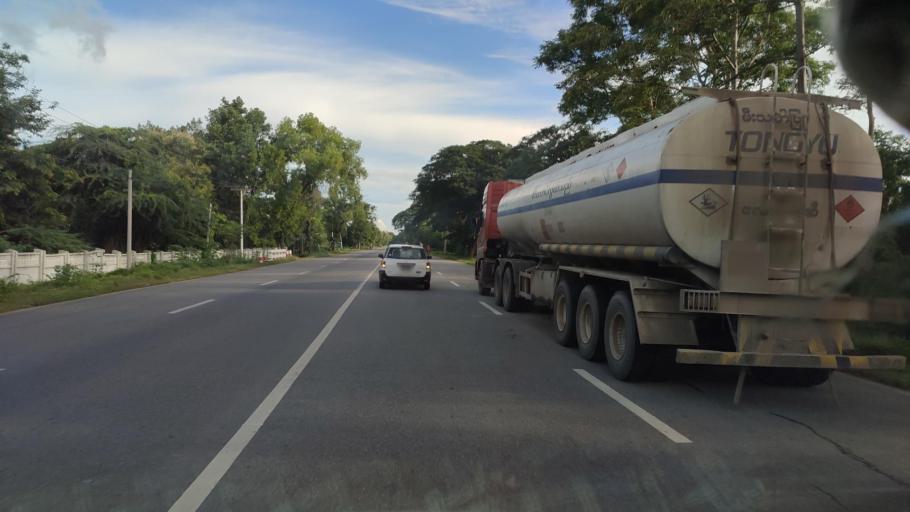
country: MM
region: Mandalay
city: Yamethin
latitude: 20.1575
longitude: 96.1913
